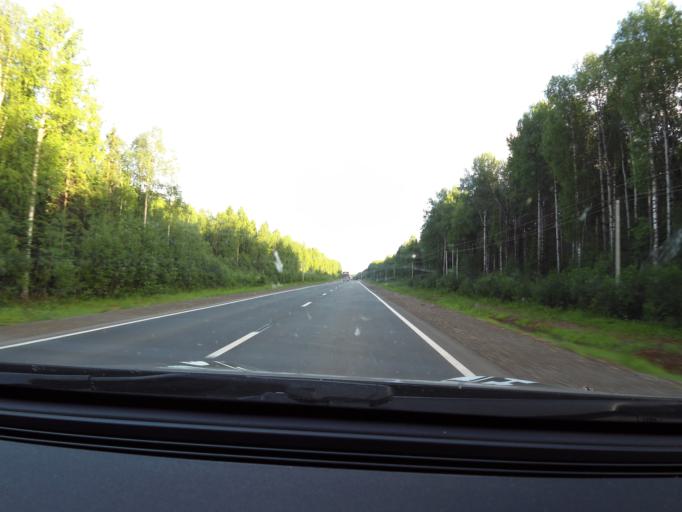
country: RU
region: Perm
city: Siva
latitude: 58.5679
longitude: 53.8892
